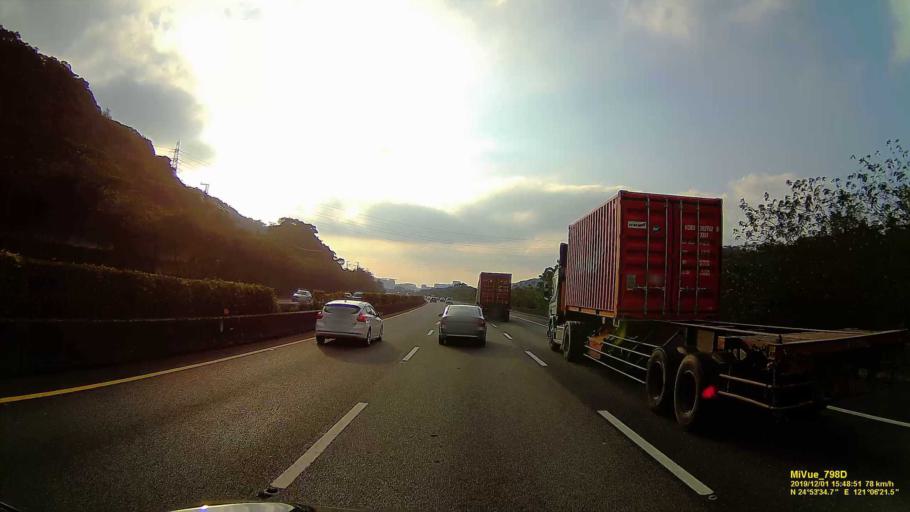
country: TW
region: Taiwan
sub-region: Hsinchu
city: Zhubei
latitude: 24.8932
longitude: 121.1054
